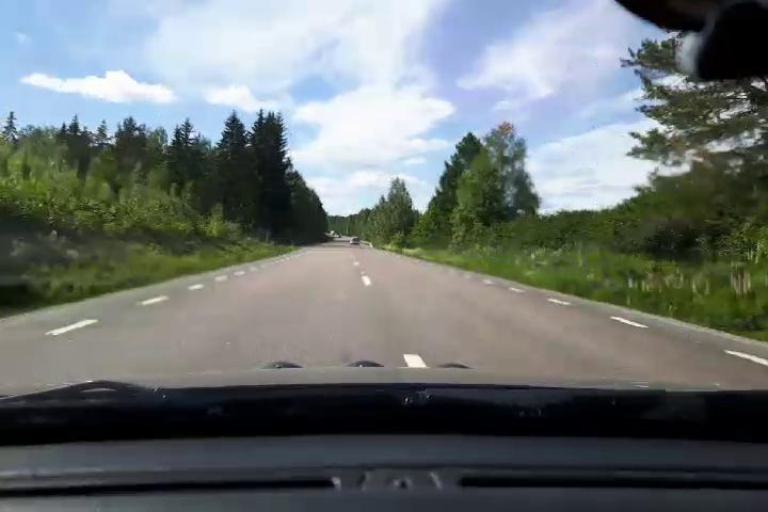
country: SE
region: Gaevleborg
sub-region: Bollnas Kommun
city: Kilafors
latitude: 61.2940
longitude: 16.4957
